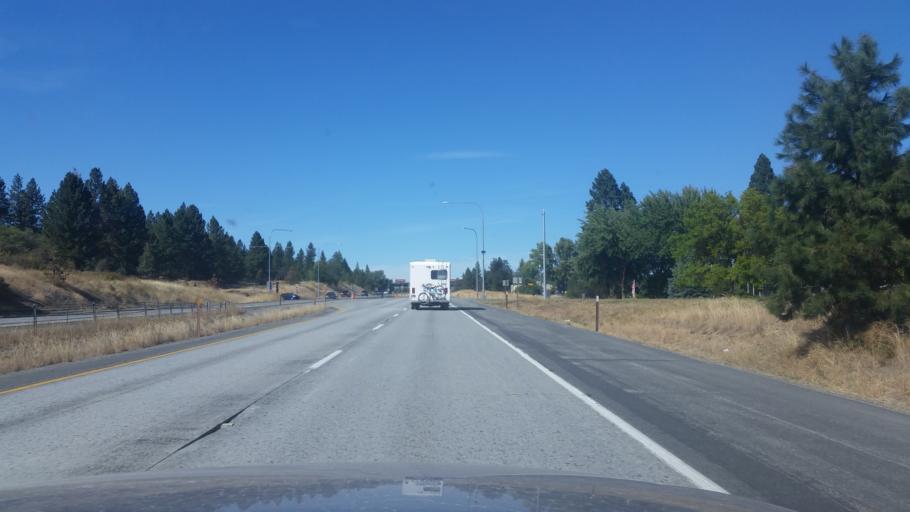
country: US
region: Washington
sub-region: Spokane County
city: Spokane
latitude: 47.6395
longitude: -117.4478
